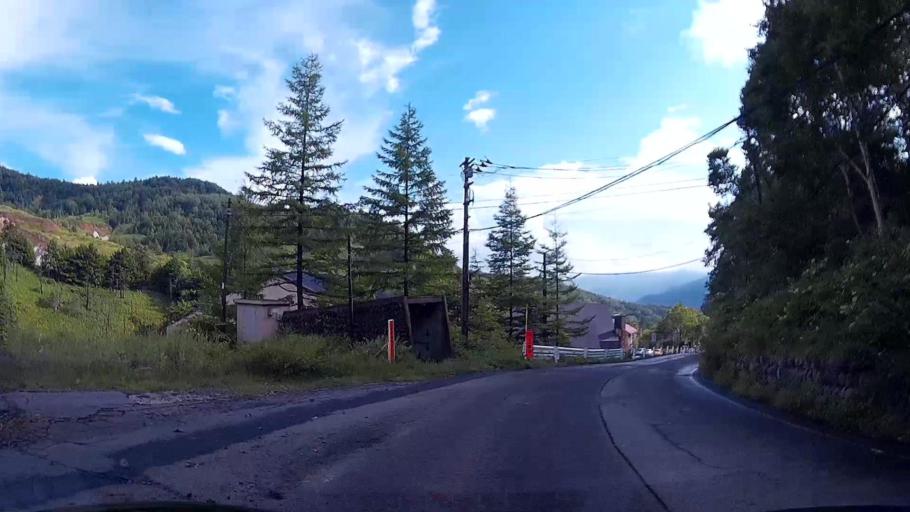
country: JP
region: Nagano
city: Nakano
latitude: 36.6365
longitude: 138.5092
